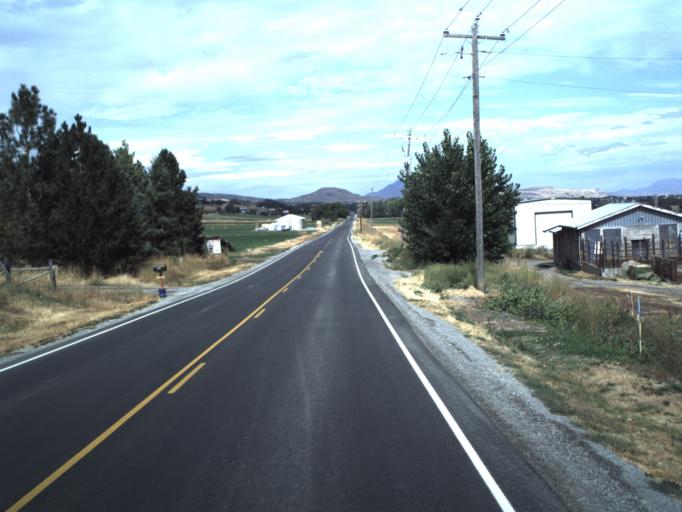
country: US
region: Utah
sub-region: Cache County
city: Wellsville
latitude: 41.6739
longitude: -111.9563
